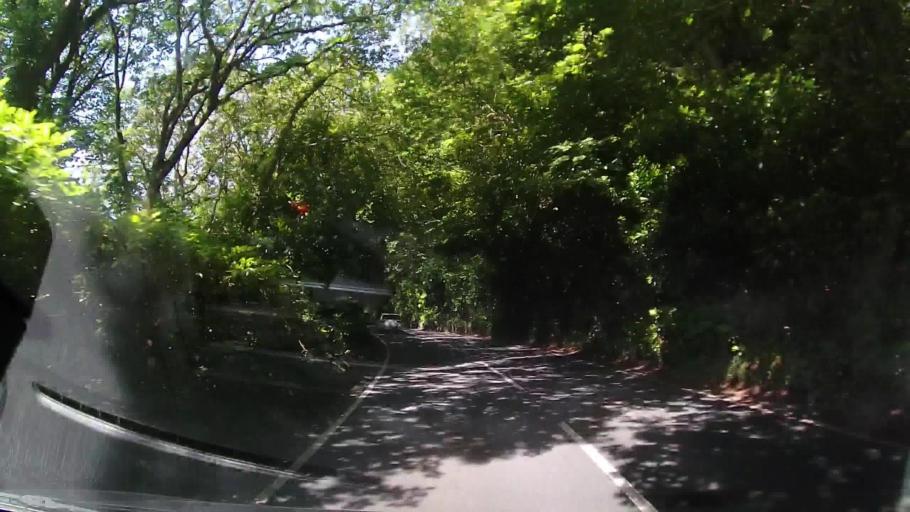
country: GB
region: Wales
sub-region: Gwynedd
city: Tywyn
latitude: 52.5555
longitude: -3.9852
